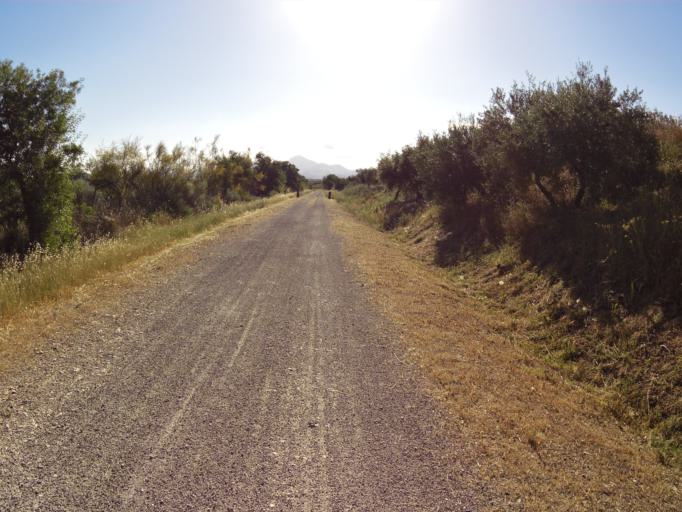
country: ES
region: Andalusia
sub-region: Province of Cordoba
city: Luque
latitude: 37.5718
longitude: -4.2294
